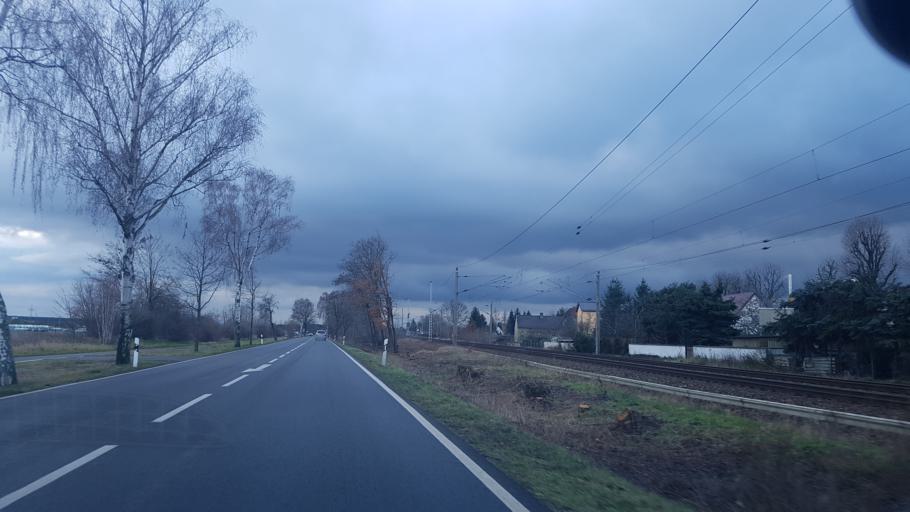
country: DE
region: Brandenburg
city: Elsterwerda
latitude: 51.4292
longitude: 13.5025
